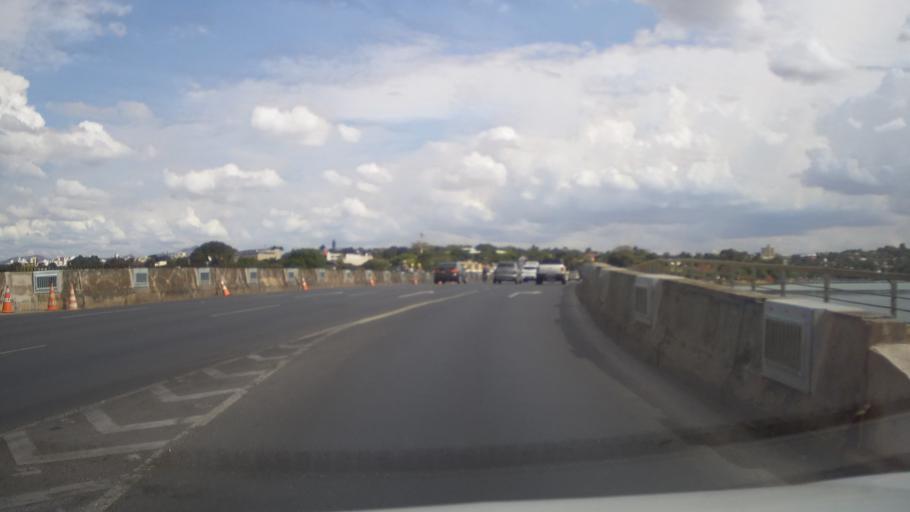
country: BR
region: Minas Gerais
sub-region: Belo Horizonte
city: Belo Horizonte
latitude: -19.8446
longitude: -43.9672
